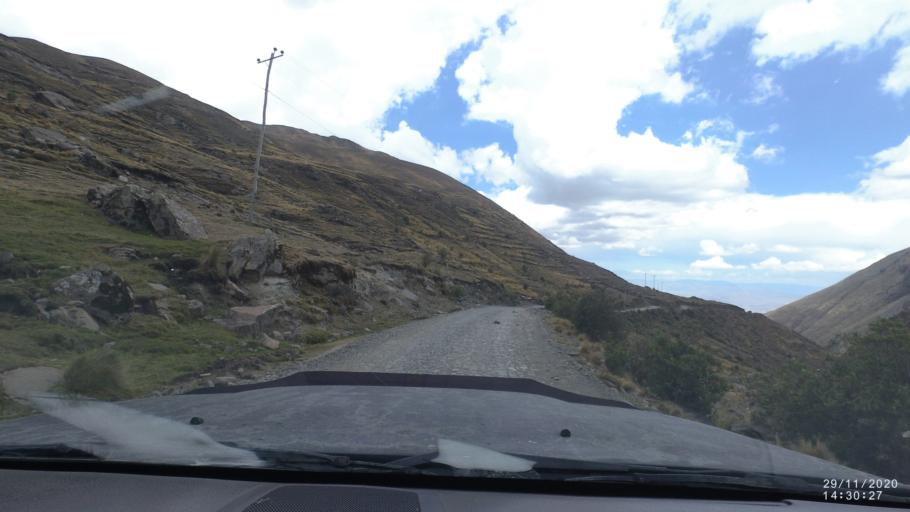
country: BO
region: Cochabamba
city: Sipe Sipe
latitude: -17.2637
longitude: -66.3488
